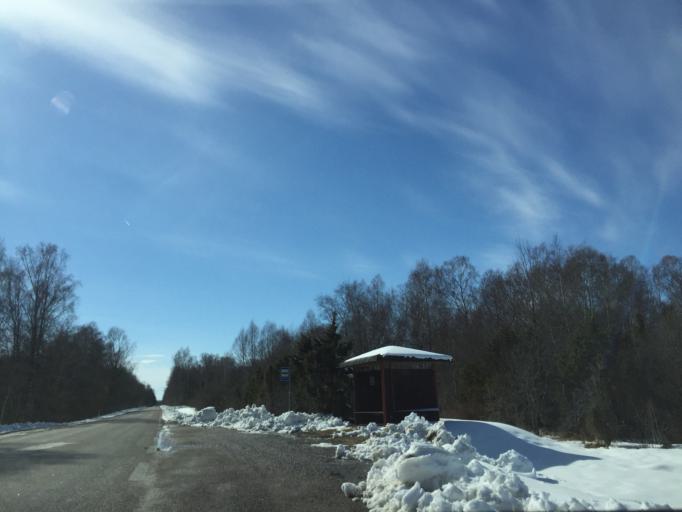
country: EE
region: Saare
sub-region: Orissaare vald
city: Orissaare
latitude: 58.3983
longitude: 22.9790
